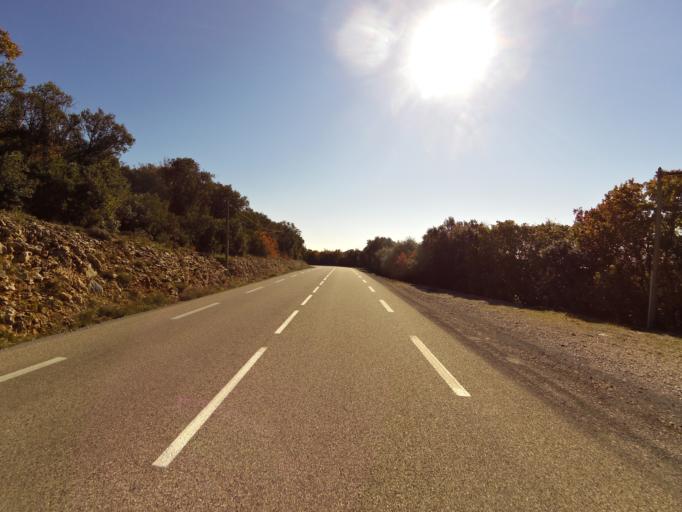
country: FR
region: Rhone-Alpes
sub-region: Departement de l'Ardeche
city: Ruoms
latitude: 44.4023
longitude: 4.4695
